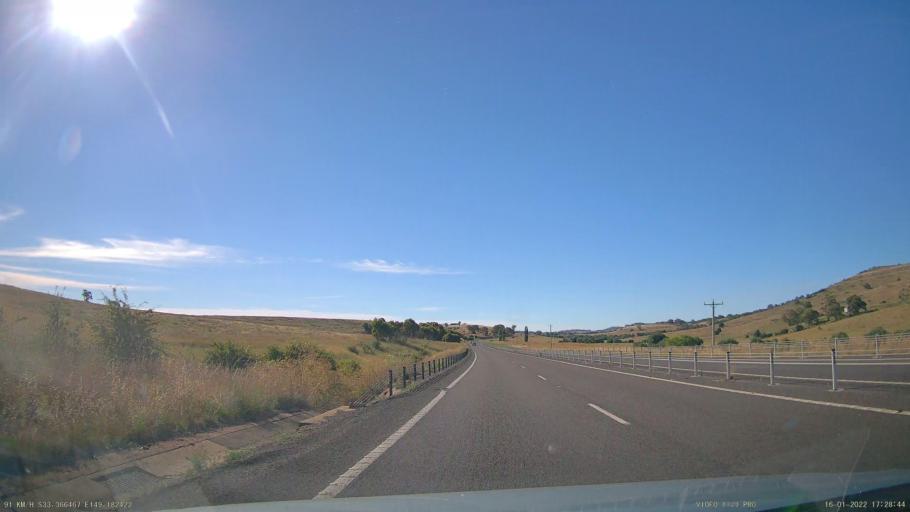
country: AU
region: New South Wales
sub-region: Blayney
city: Millthorpe
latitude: -33.3663
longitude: 149.1822
